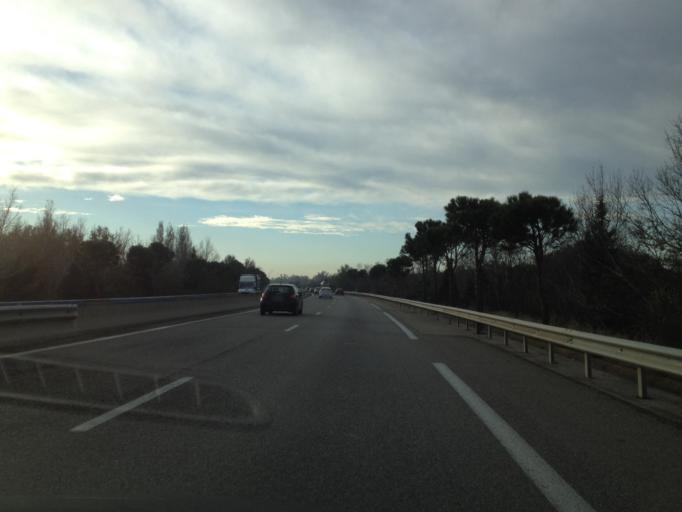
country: FR
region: Provence-Alpes-Cote d'Azur
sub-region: Departement du Vaucluse
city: Sorgues
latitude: 44.0050
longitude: 4.8633
